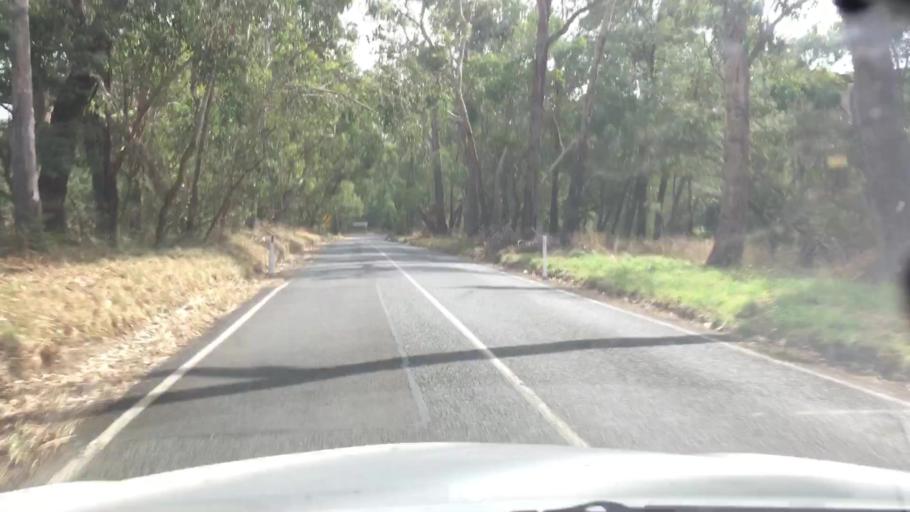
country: AU
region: Victoria
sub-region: Yarra Ranges
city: Woori Yallock
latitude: -37.8162
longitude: 145.4990
